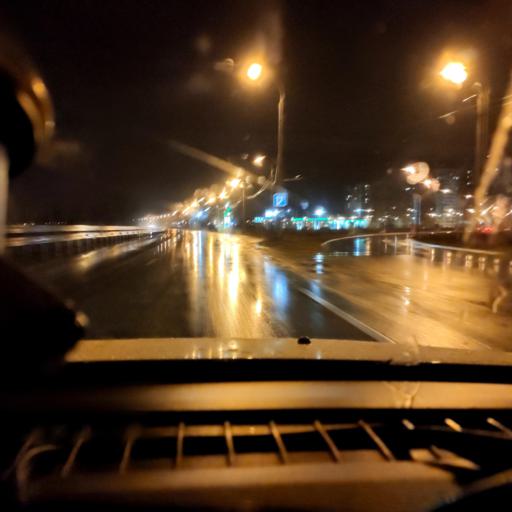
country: RU
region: Samara
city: Samara
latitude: 53.0945
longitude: 50.1551
